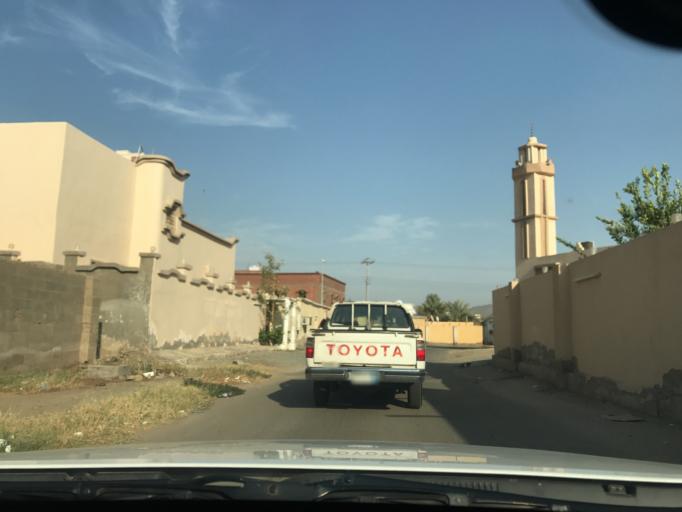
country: SA
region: Makkah
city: Al Jumum
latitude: 21.4406
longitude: 39.5220
